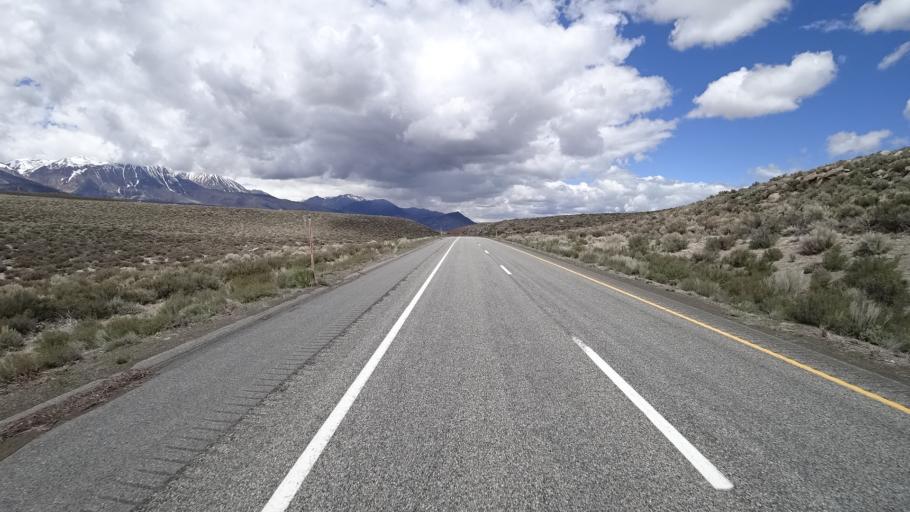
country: US
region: California
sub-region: Mono County
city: Mammoth Lakes
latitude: 37.8460
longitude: -119.0795
